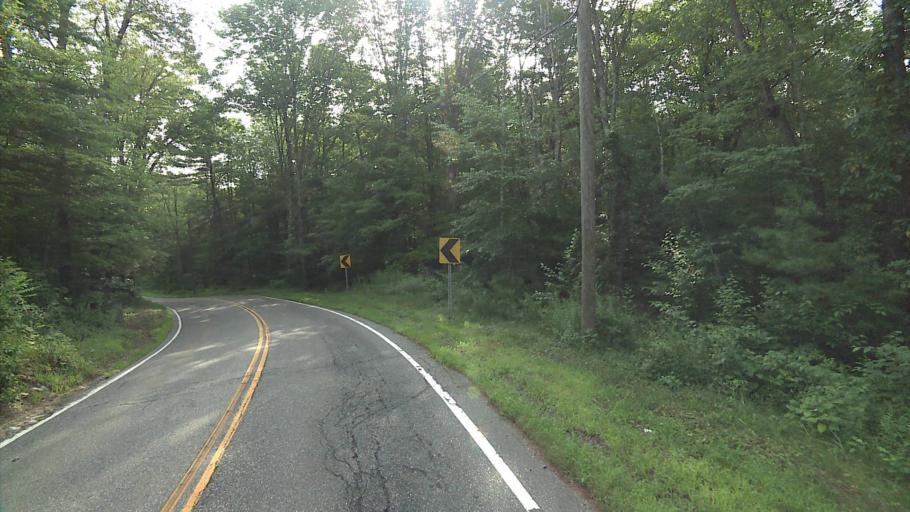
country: US
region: Massachusetts
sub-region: Hampden County
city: Holland
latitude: 41.9840
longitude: -72.1036
